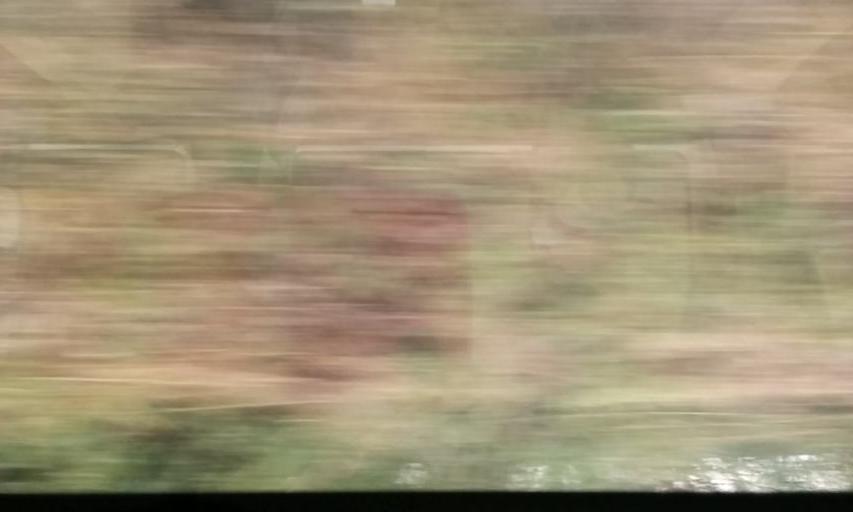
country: JP
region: Nagano
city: Matsumoto
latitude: 36.2565
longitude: 137.9506
